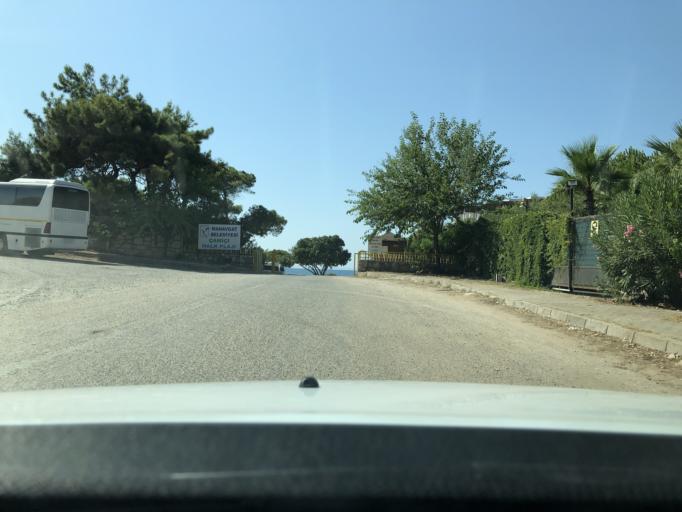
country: TR
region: Antalya
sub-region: Manavgat
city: Manavgat
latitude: 36.7583
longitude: 31.4228
